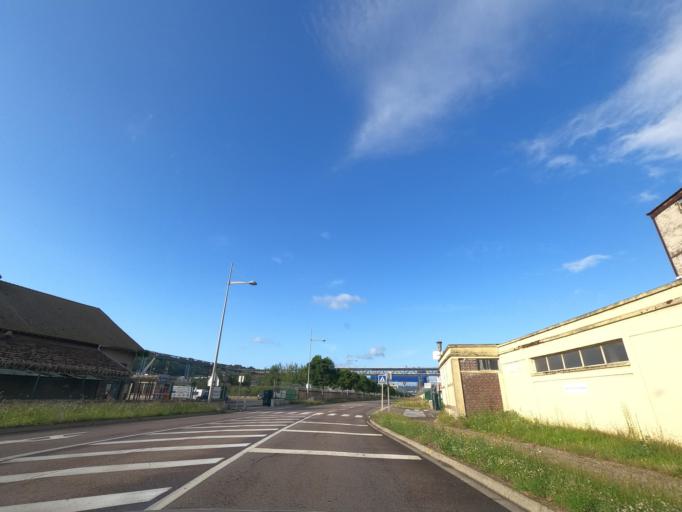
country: FR
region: Haute-Normandie
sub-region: Departement de la Seine-Maritime
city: Canteleu
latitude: 49.4209
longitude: 1.0252
